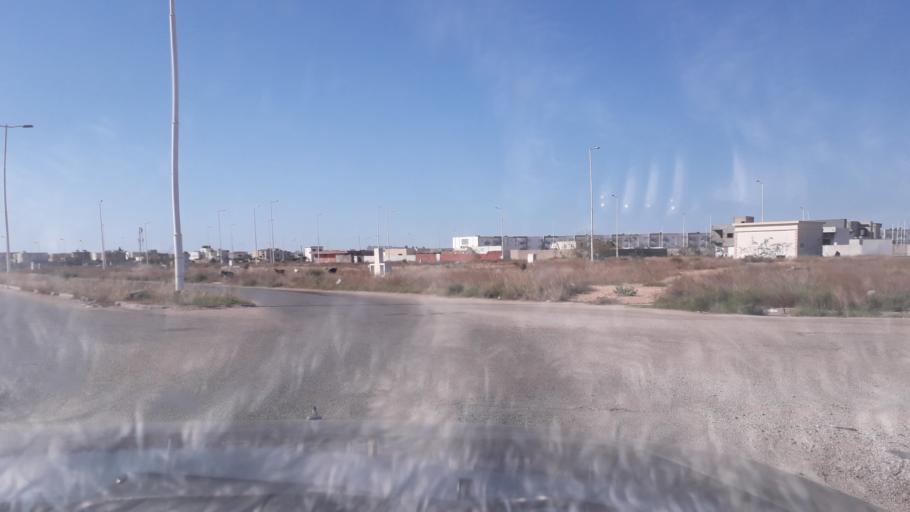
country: TN
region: Safaqis
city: Al Qarmadah
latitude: 34.8343
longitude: 10.7539
